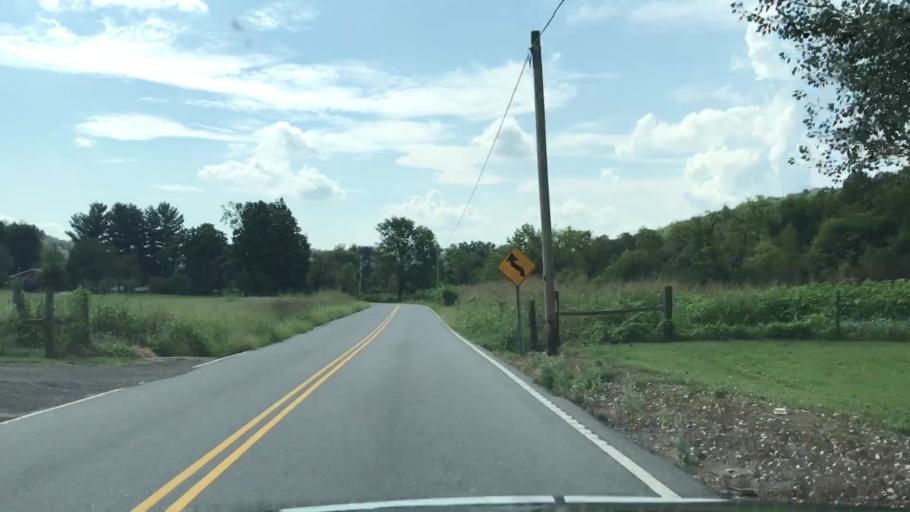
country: US
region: Tennessee
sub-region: Trousdale County
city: Hartsville
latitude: 36.4757
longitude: -86.1829
